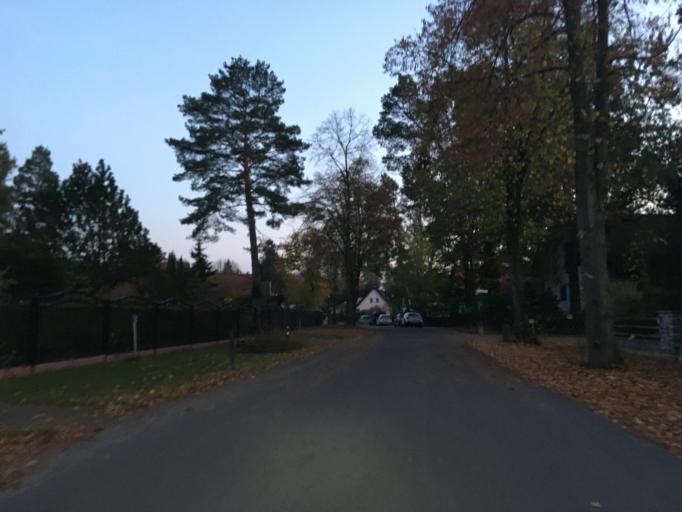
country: DE
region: Brandenburg
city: Birkenwerder
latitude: 52.6828
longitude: 13.3205
